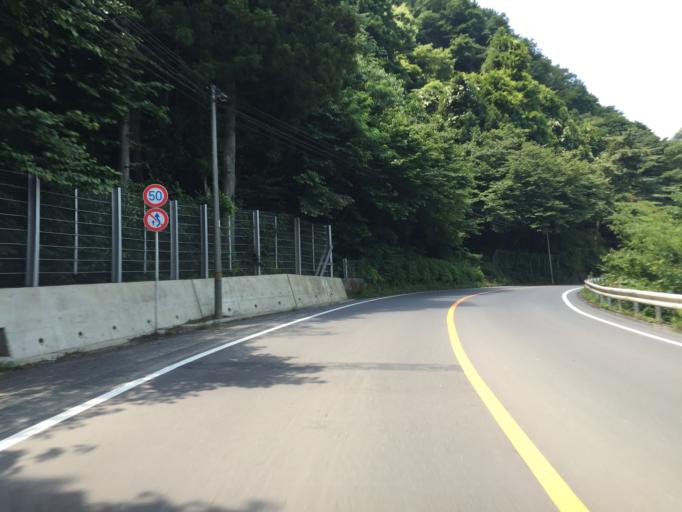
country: JP
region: Miyagi
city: Marumori
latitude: 37.7791
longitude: 140.8129
